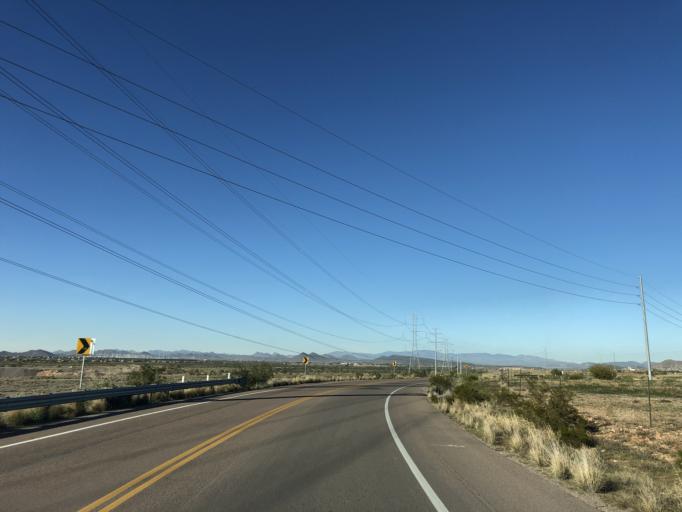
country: US
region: Arizona
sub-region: Maricopa County
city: Sun City West
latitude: 33.6772
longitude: -112.2998
